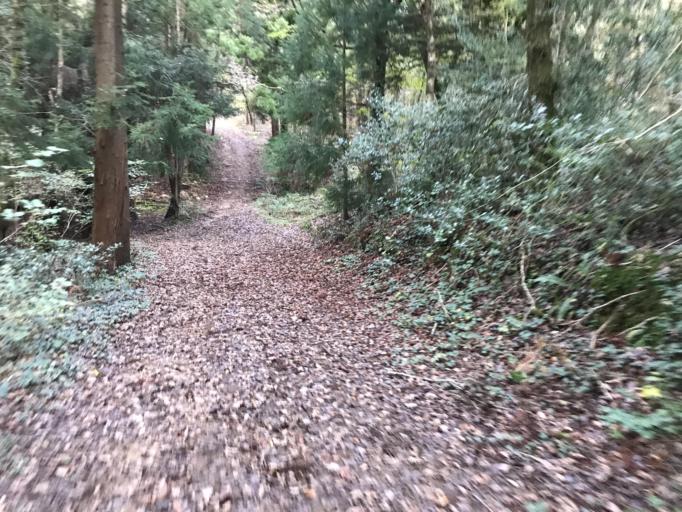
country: FR
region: Brittany
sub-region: Departement du Finistere
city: Hopital-Camfrout
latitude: 48.3332
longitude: -4.2226
